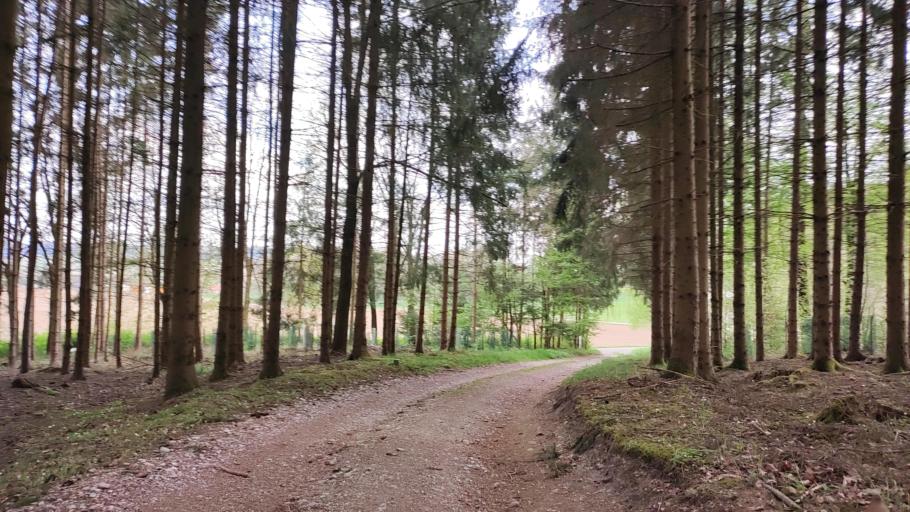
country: DE
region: Bavaria
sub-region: Swabia
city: Zusmarshausen
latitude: 48.3959
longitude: 10.5741
